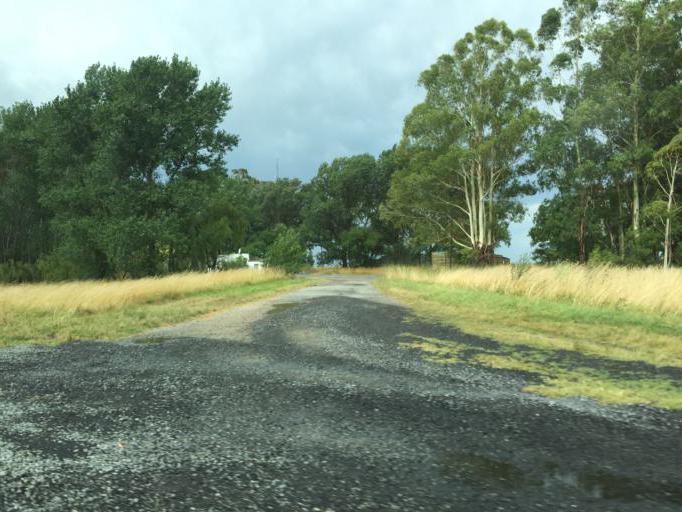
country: AR
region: Buenos Aires
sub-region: Partido de Rauch
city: Rauch
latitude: -36.9761
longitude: -58.9971
